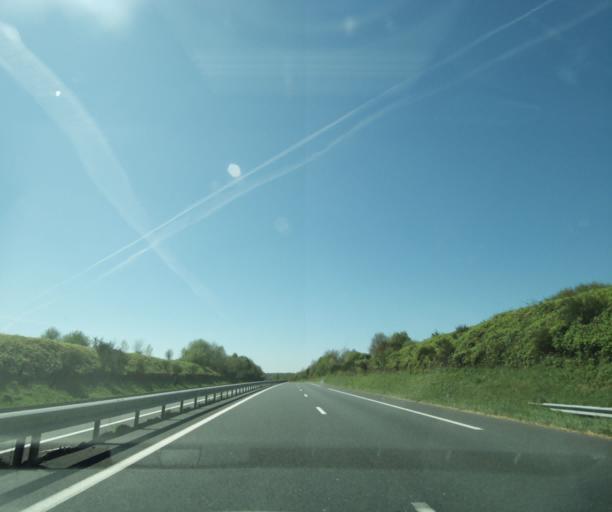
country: FR
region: Centre
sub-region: Departement de l'Indre
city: Chantome
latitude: 46.4153
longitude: 1.4673
